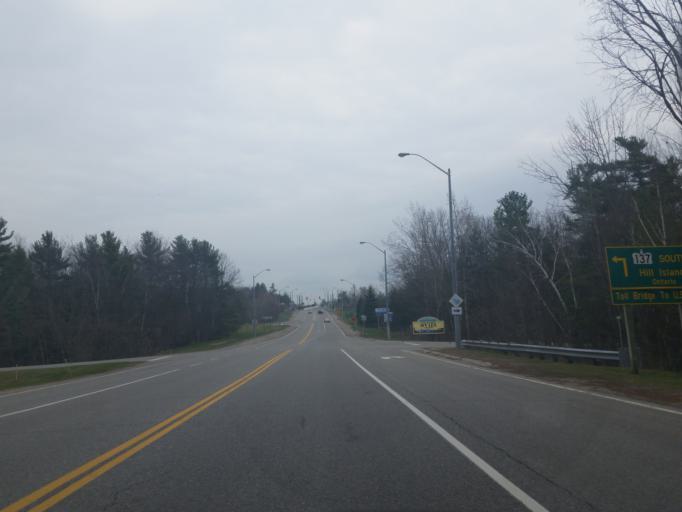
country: US
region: New York
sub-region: Jefferson County
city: Alexandria Bay
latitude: 44.3694
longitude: -75.9854
